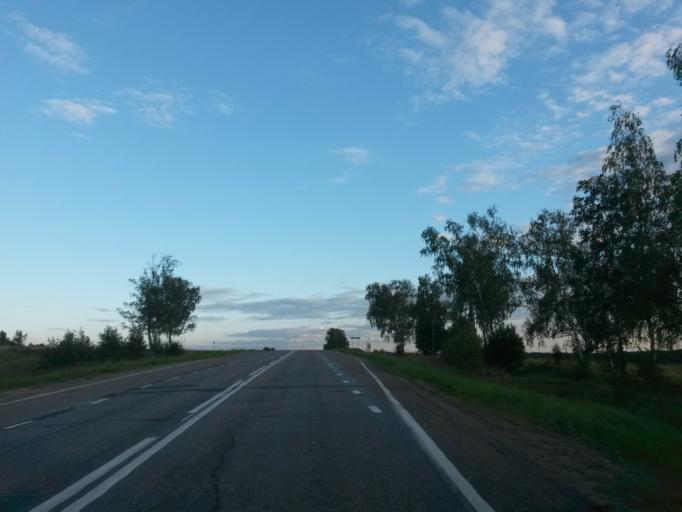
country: RU
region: Jaroslavl
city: Gavrilov-Yam
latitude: 57.4488
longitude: 39.9140
